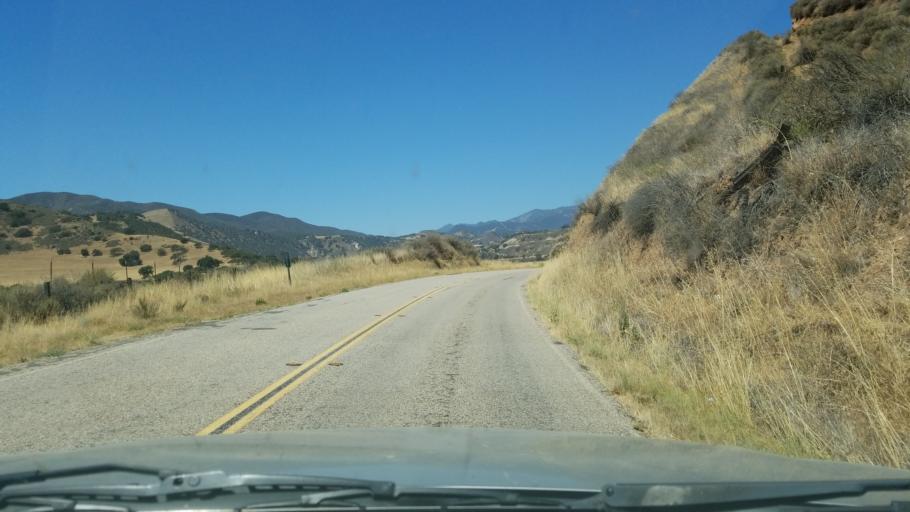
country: US
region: California
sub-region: Monterey County
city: Greenfield
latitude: 36.2700
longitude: -121.3359
